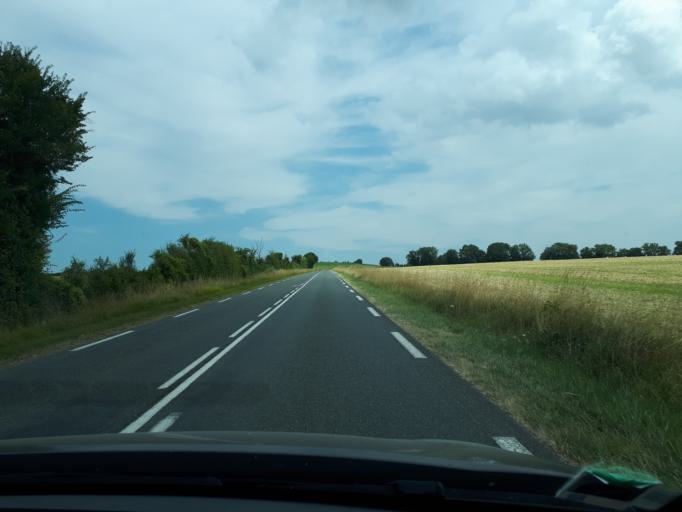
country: FR
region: Centre
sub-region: Departement du Cher
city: Rians
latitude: 47.2307
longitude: 2.6404
